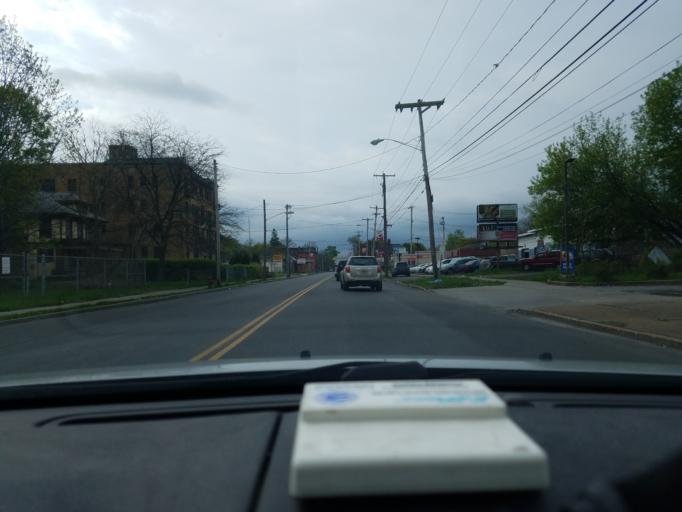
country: US
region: New York
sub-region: Onondaga County
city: Syracuse
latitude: 43.0327
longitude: -76.1489
